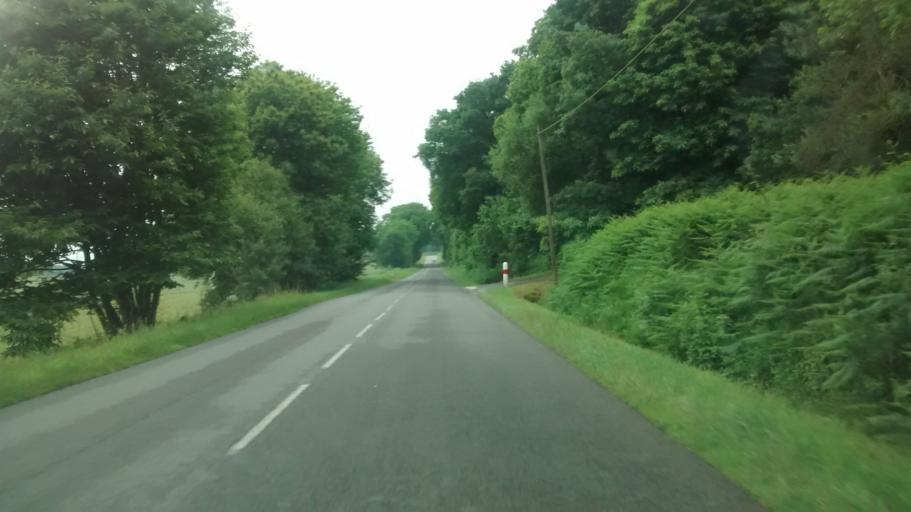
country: FR
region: Brittany
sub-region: Departement du Morbihan
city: Serent
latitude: 47.8188
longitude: -2.4718
